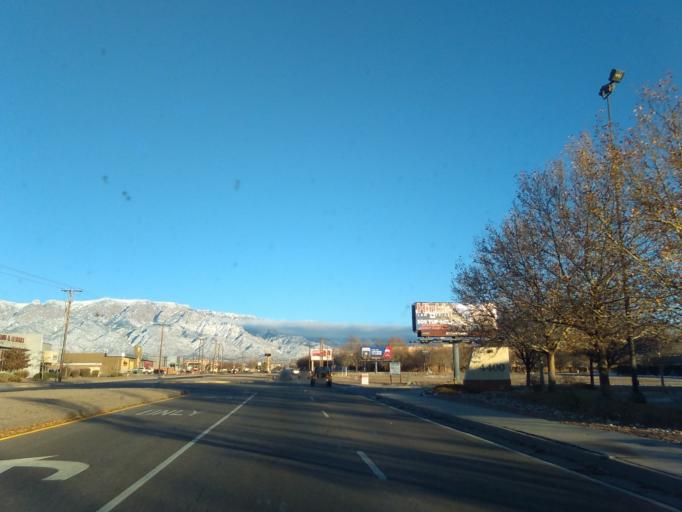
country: US
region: New Mexico
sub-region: Bernalillo County
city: North Valley
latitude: 35.1845
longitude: -106.5977
